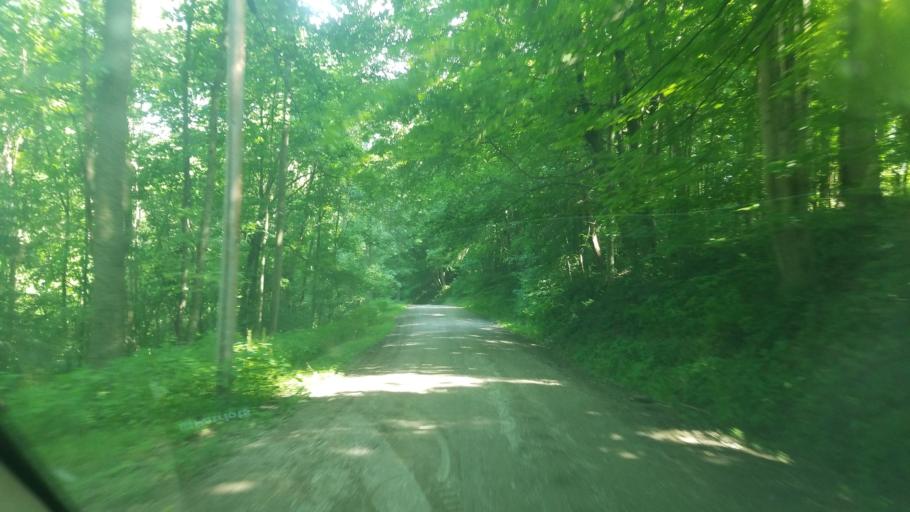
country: US
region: Ohio
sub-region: Holmes County
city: Millersburg
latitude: 40.4701
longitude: -81.9637
